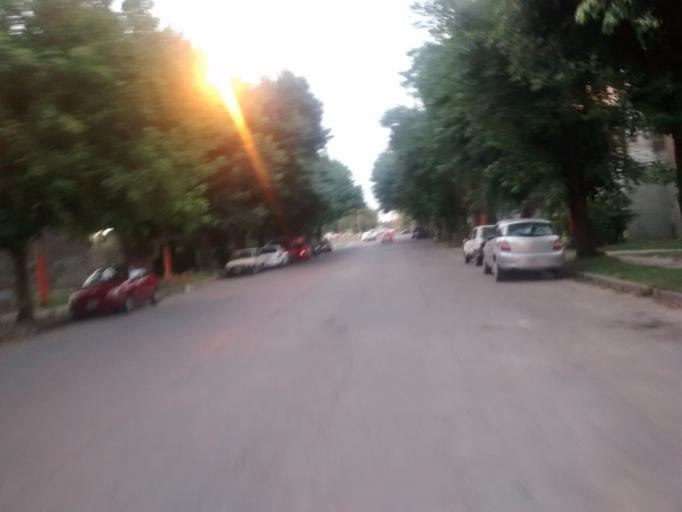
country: AR
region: Buenos Aires
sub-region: Partido de La Plata
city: La Plata
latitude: -34.9416
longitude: -57.9243
